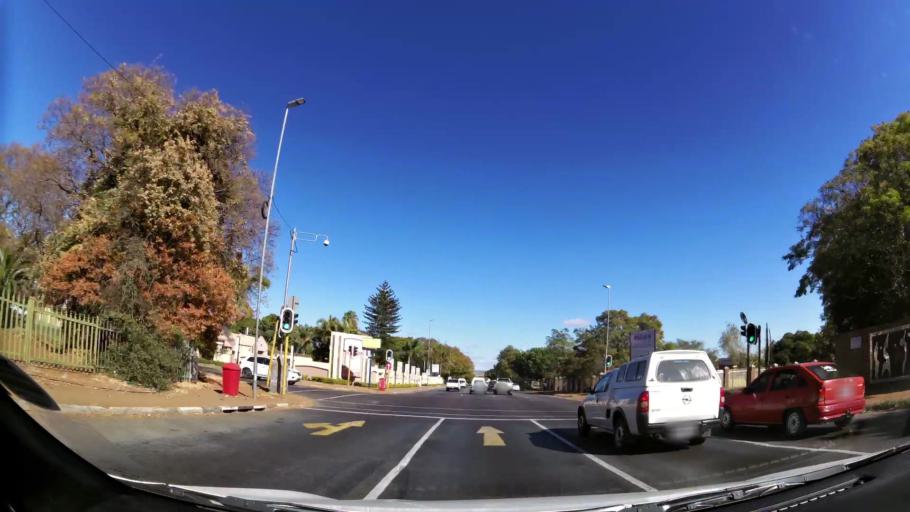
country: ZA
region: Limpopo
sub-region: Capricorn District Municipality
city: Polokwane
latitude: -23.9087
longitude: 29.4668
